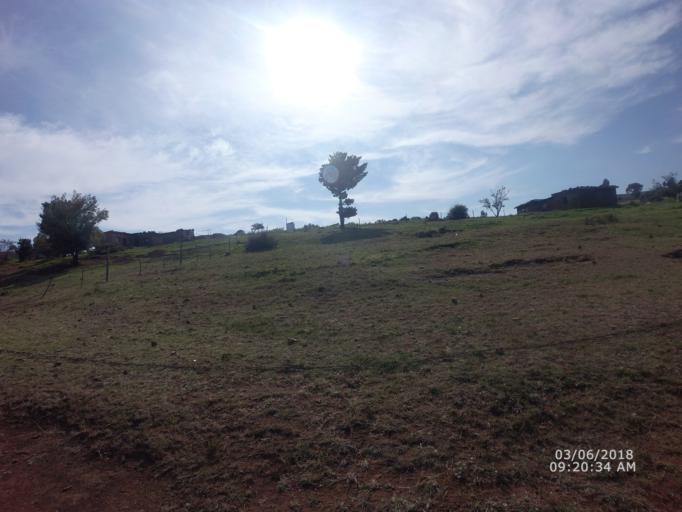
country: LS
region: Berea
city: Teyateyaneng
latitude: -29.2288
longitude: 27.8647
